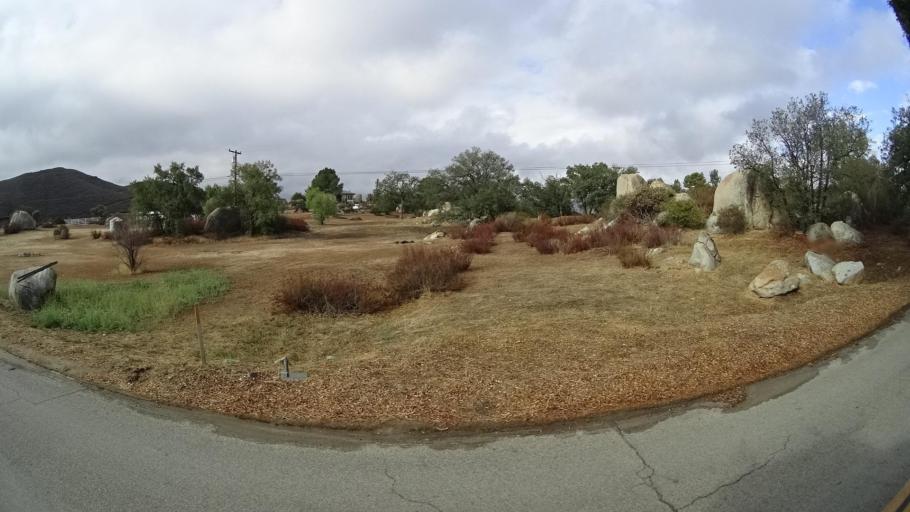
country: MX
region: Baja California
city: Tecate
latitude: 32.6340
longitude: -116.6350
